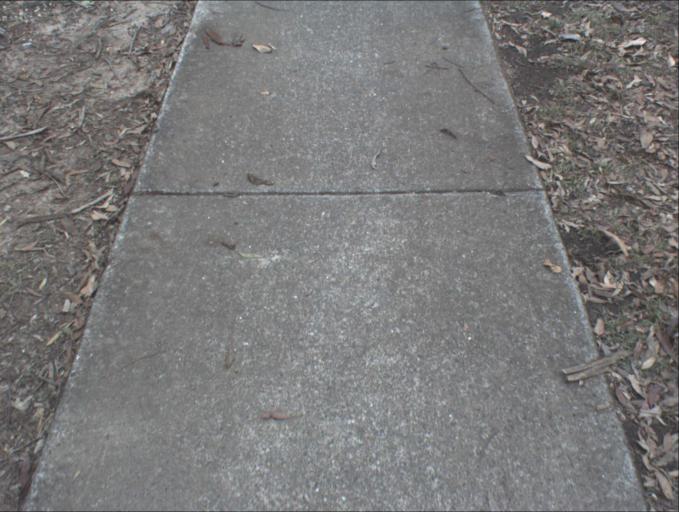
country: AU
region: Queensland
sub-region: Logan
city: Waterford West
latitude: -27.6846
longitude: 153.1007
